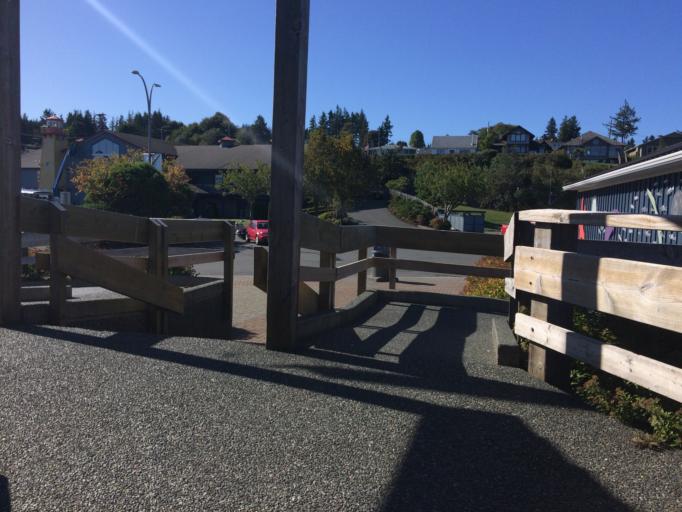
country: CA
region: British Columbia
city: Campbell River
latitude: 50.0207
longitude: -125.2362
